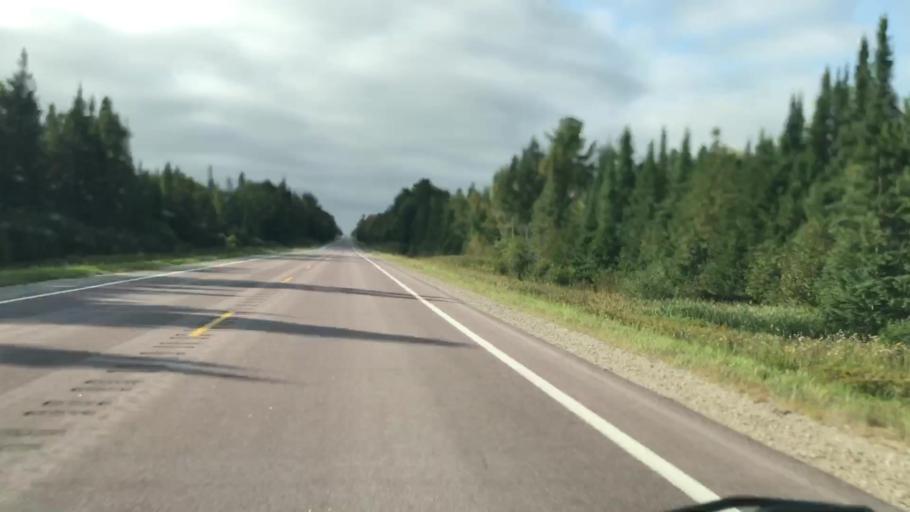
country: US
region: Michigan
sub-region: Luce County
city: Newberry
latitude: 46.2969
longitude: -85.5689
